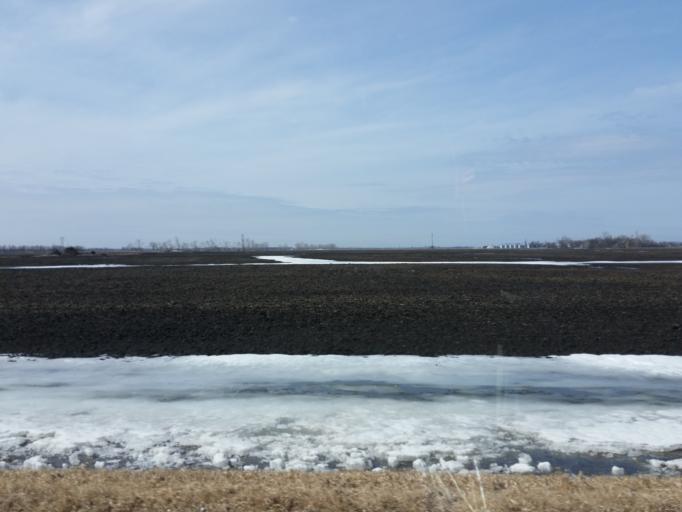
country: US
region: North Dakota
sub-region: Walsh County
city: Grafton
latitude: 48.2908
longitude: -97.2547
